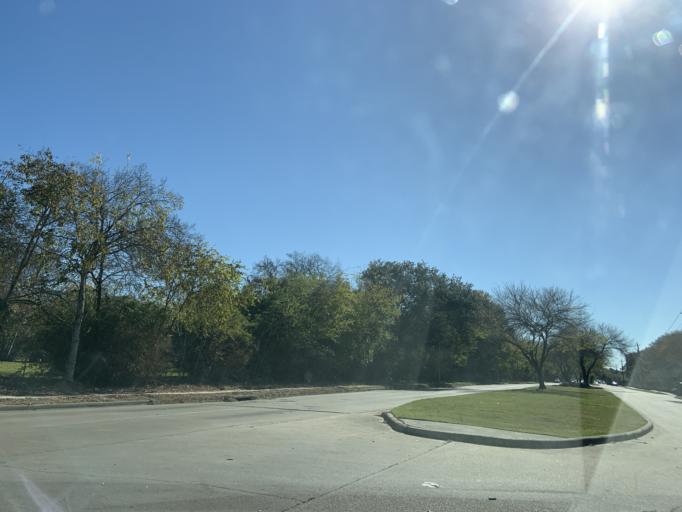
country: US
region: Texas
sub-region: Harris County
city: Bellaire
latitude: 29.6834
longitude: -95.5088
